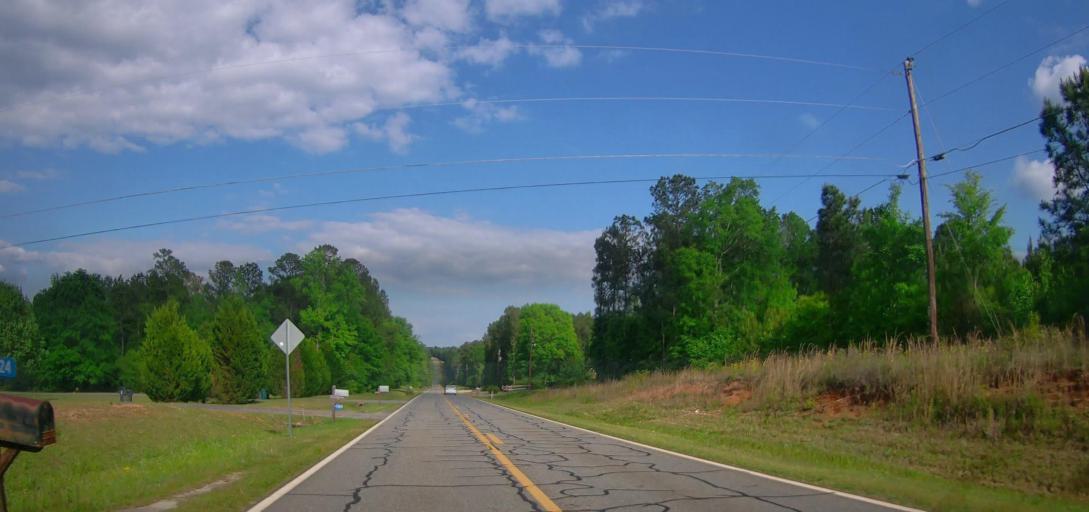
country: US
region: Georgia
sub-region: Baldwin County
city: Hardwick
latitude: 33.0638
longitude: -83.1662
